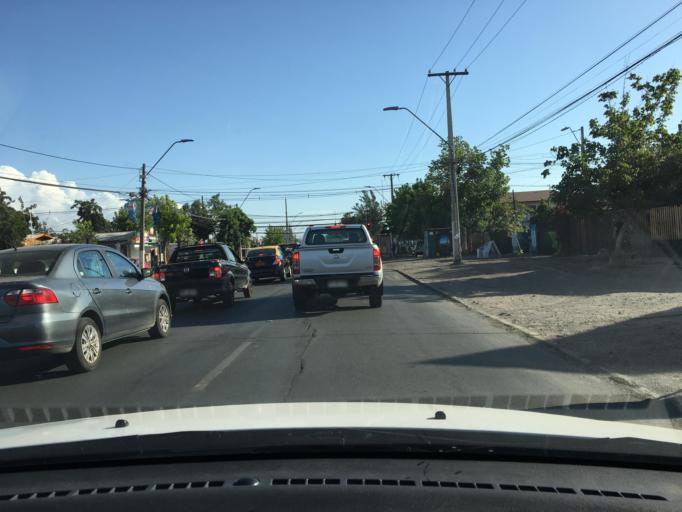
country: CL
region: Santiago Metropolitan
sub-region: Provincia de Santiago
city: Villa Presidente Frei, Nunoa, Santiago, Chile
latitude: -33.4897
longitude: -70.6064
